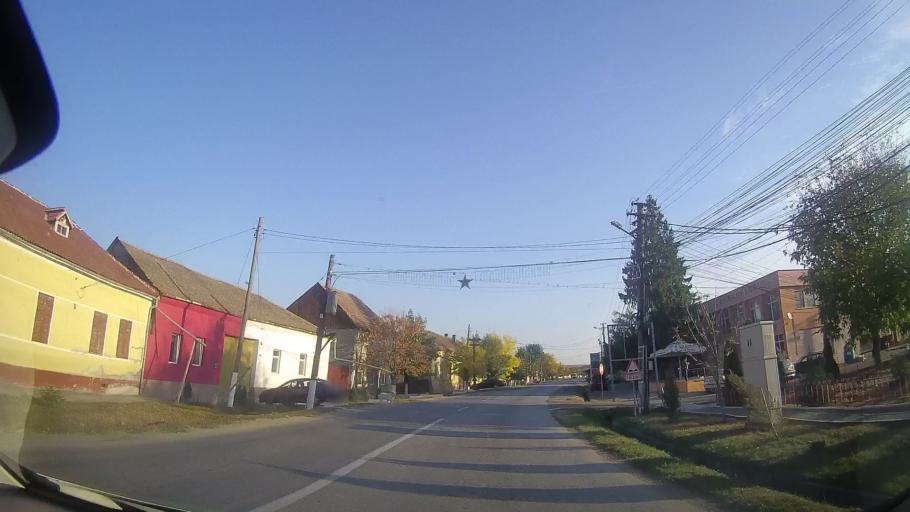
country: RO
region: Timis
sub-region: Comuna Pischia
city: Pischia
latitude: 45.9041
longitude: 21.3402
